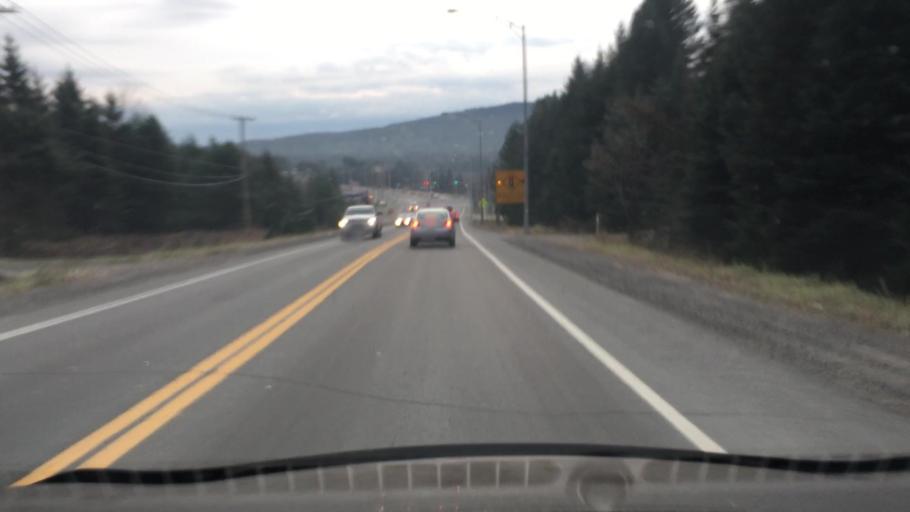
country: CA
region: Quebec
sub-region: Laurentides
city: Saint-Sauveur
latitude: 45.9053
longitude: -74.2490
